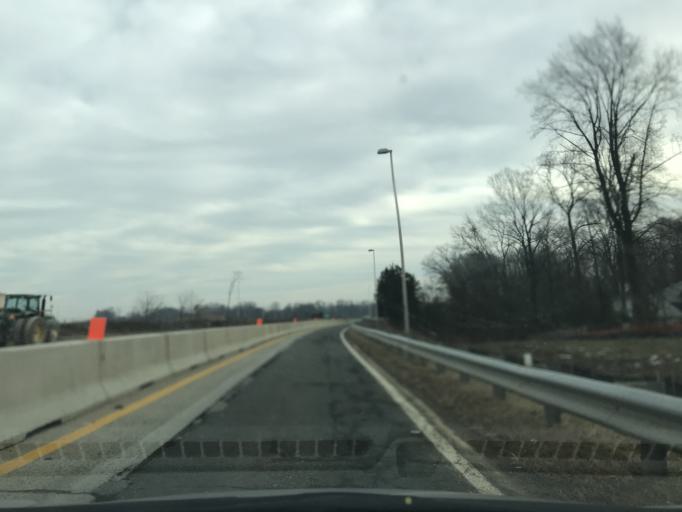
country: US
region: Virginia
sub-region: Fairfax County
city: Oakton
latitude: 38.8670
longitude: -77.3131
